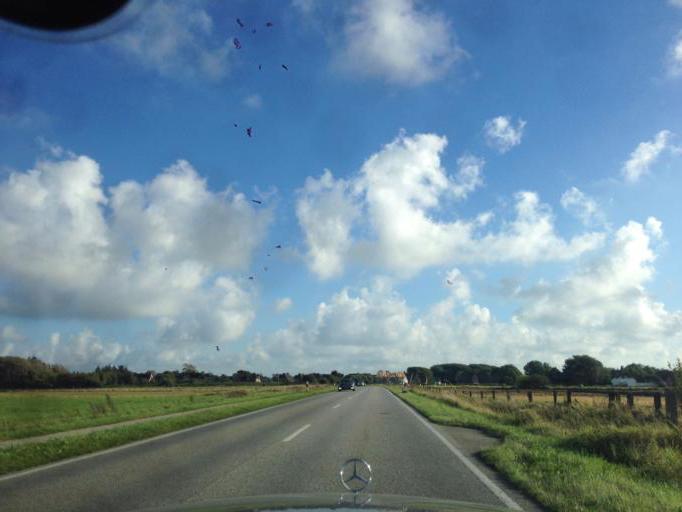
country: DE
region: Schleswig-Holstein
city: Sylt-Ost
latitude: 54.8769
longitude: 8.3917
